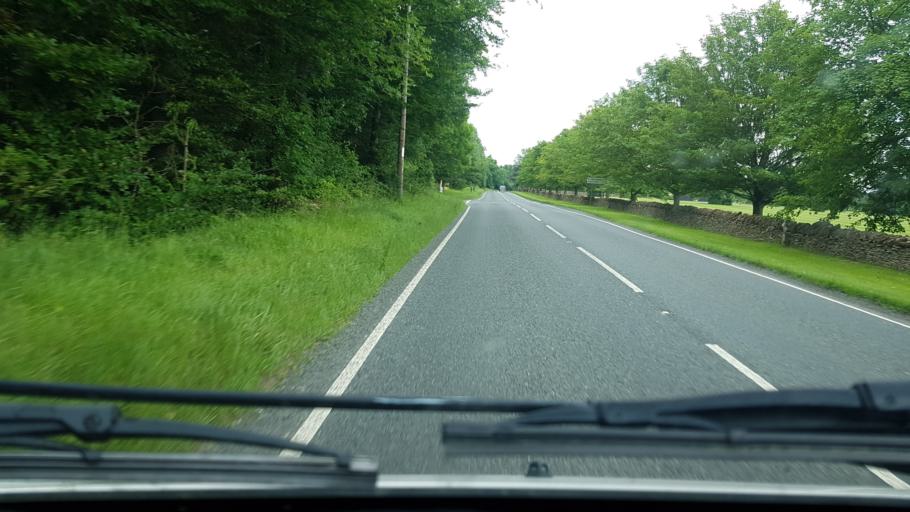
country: GB
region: England
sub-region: Gloucestershire
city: Donnington
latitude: 51.9634
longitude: -1.7525
